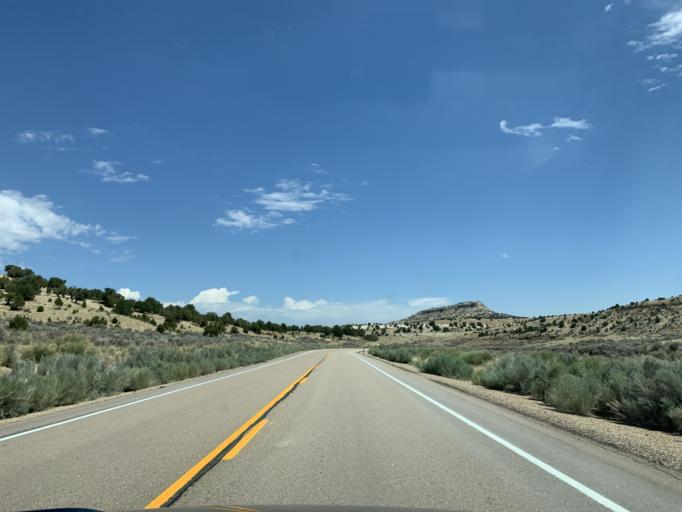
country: US
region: Utah
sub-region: Duchesne County
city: Duchesne
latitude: 39.9041
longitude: -110.2341
